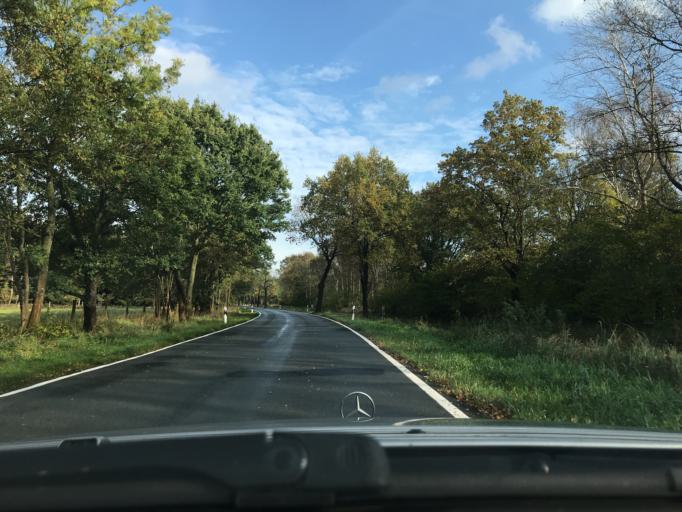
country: DE
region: Mecklenburg-Vorpommern
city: Kroslin
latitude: 54.1413
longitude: 13.7893
